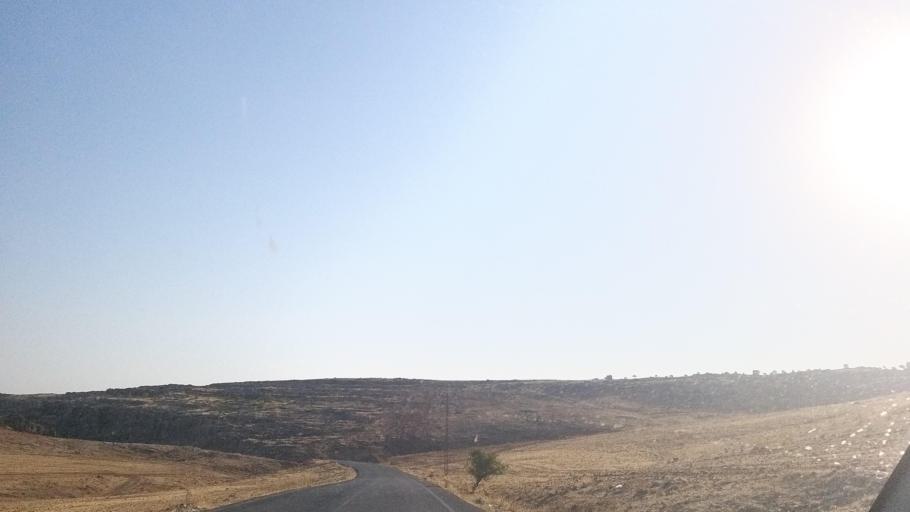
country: TR
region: Diyarbakir
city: Silvan
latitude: 38.1706
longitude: 41.0038
